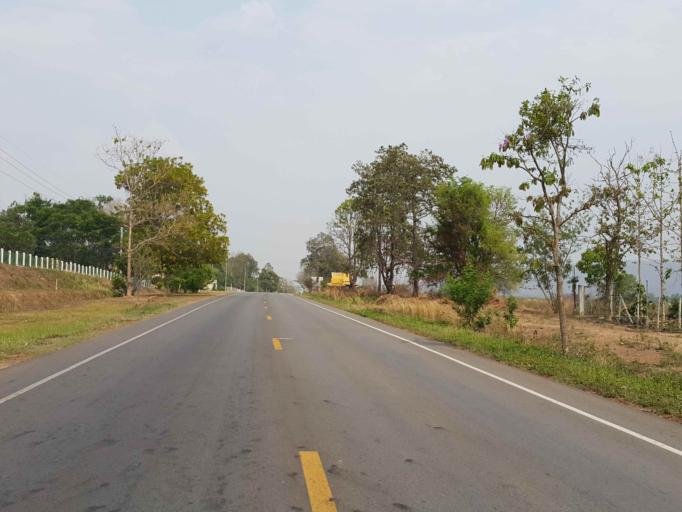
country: TH
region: Chiang Mai
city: Mae Taeng
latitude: 19.1109
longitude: 99.0256
